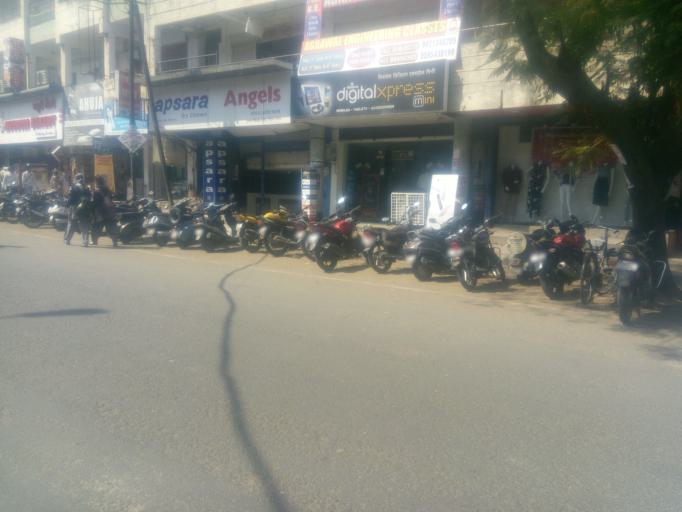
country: IN
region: Maharashtra
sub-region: Nagpur Division
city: Nagpur
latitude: 21.1642
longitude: 79.0804
